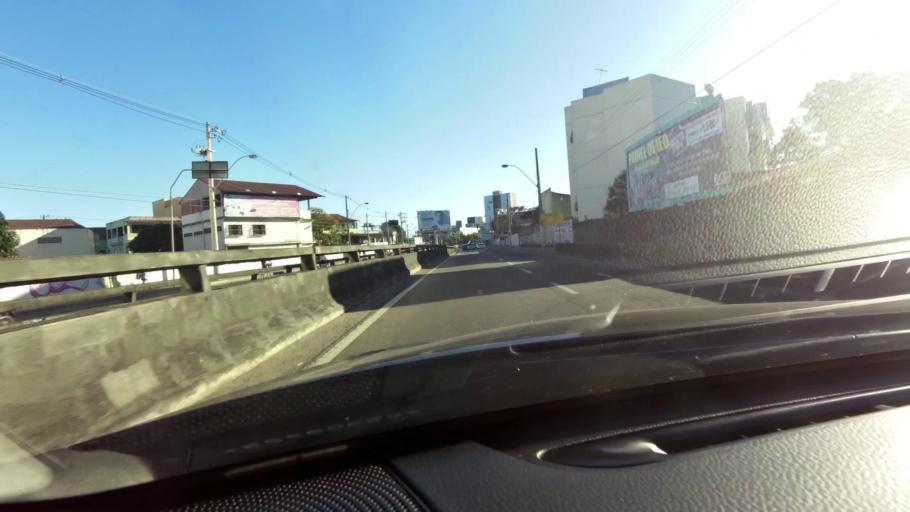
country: BR
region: Espirito Santo
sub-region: Vila Velha
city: Vila Velha
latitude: -20.3416
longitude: -40.2908
